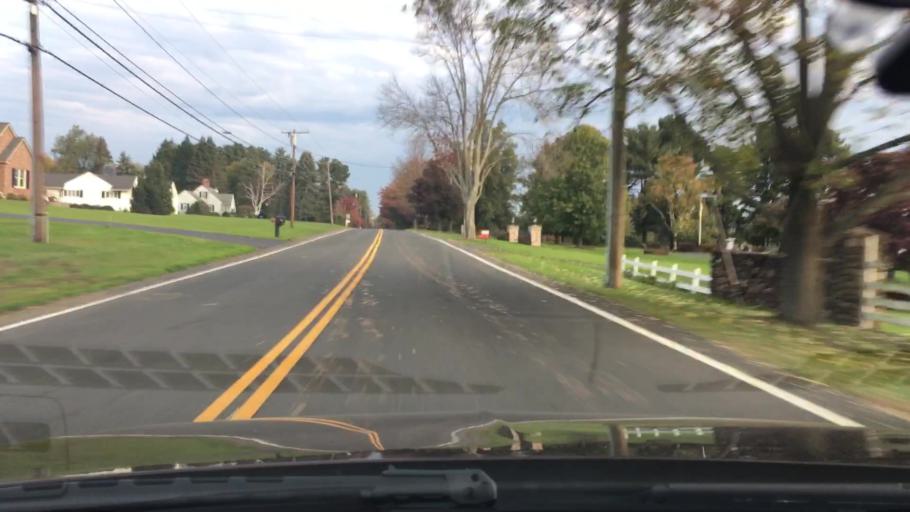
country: US
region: Massachusetts
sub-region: Hampden County
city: East Longmeadow
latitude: 42.0228
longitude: -72.4851
